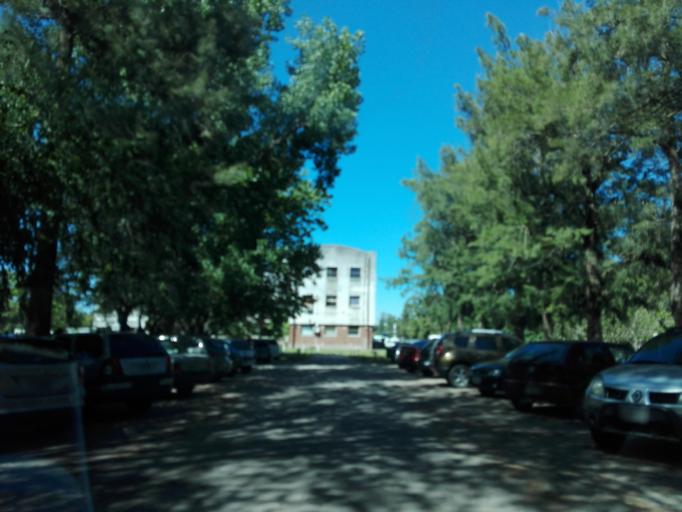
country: AR
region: Buenos Aires
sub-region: Partido de La Plata
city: La Plata
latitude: -34.8988
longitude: -57.9283
